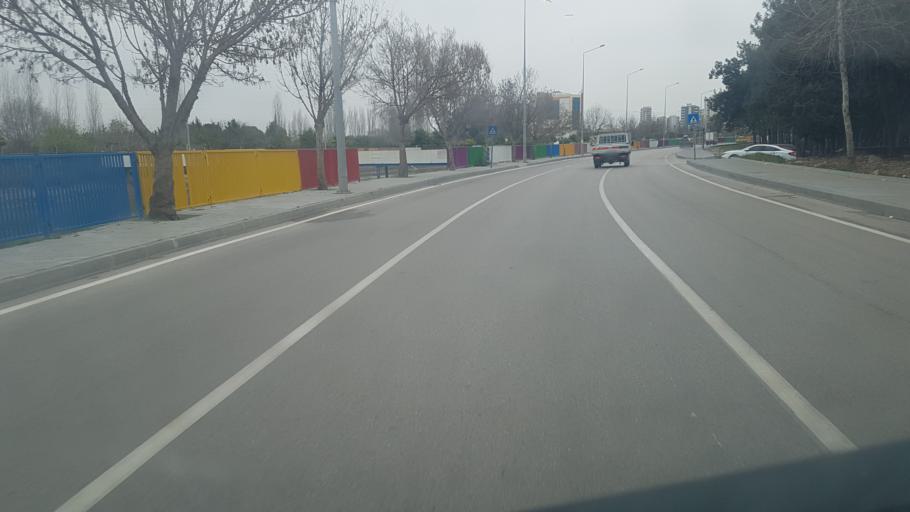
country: TR
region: Adana
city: Adana
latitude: 37.0126
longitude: 35.3484
